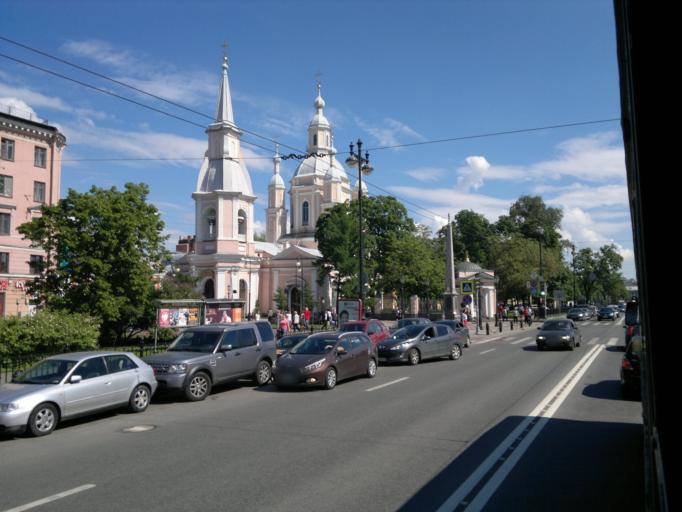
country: RU
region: St.-Petersburg
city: Vasyl'evsky Ostrov
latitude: 59.9391
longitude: 30.2827
